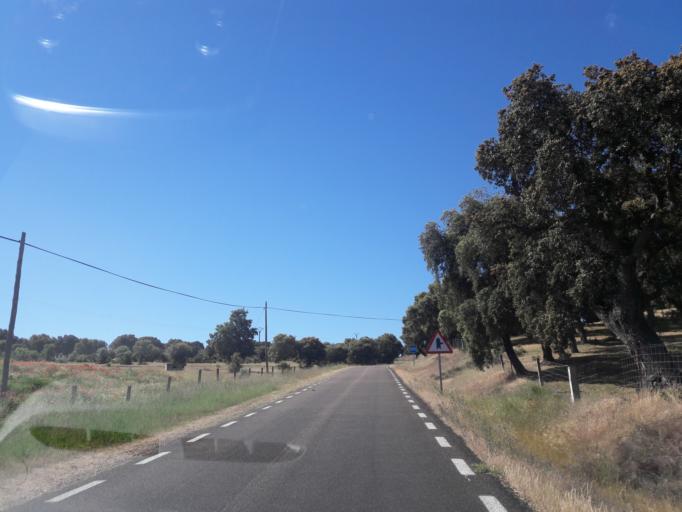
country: ES
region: Castille and Leon
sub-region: Provincia de Salamanca
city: Juzbado
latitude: 41.0668
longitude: -5.8990
